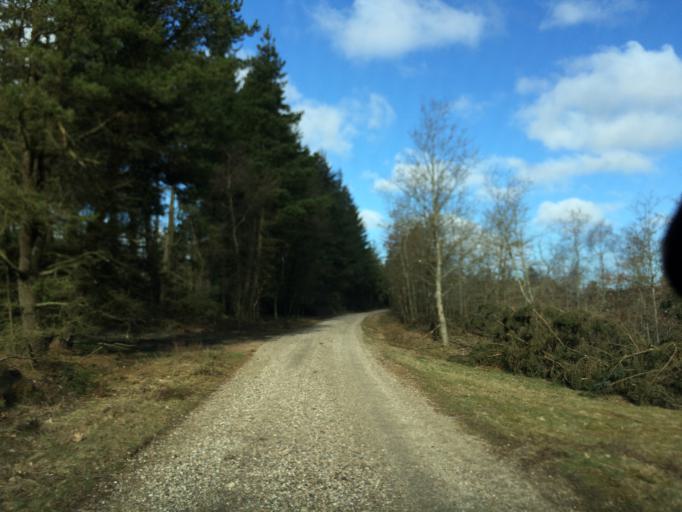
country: DK
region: Central Jutland
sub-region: Holstebro Kommune
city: Ulfborg
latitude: 56.2746
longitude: 8.4252
